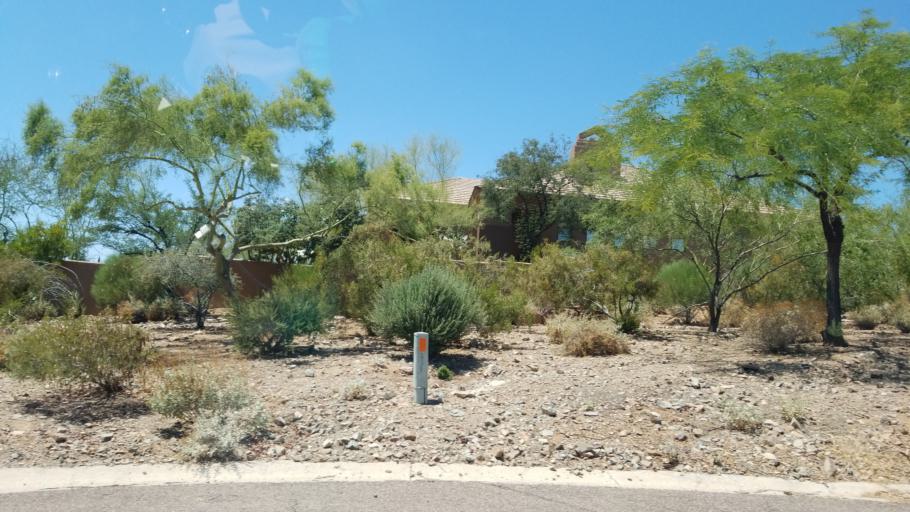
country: US
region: Arizona
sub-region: Maricopa County
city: Paradise Valley
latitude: 33.6173
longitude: -112.0165
